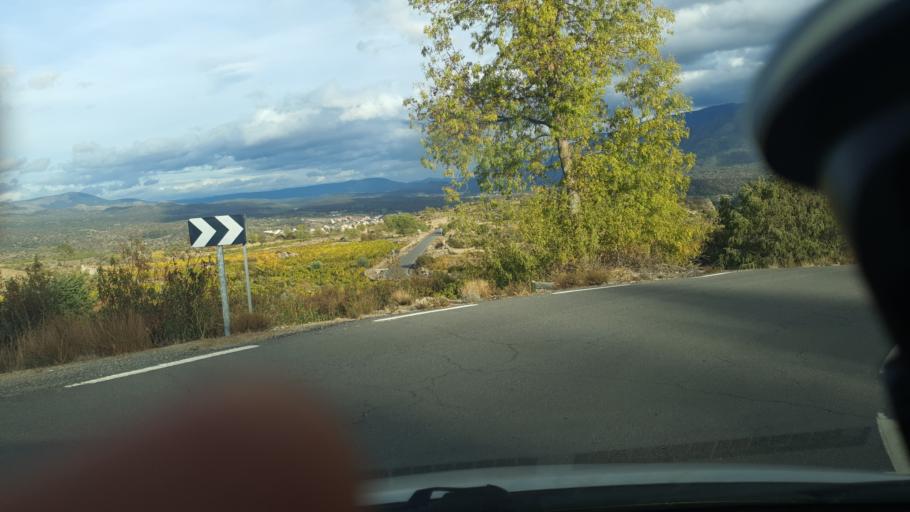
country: ES
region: Castille and Leon
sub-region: Provincia de Avila
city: Burgohondo
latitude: 40.4096
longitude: -4.8201
